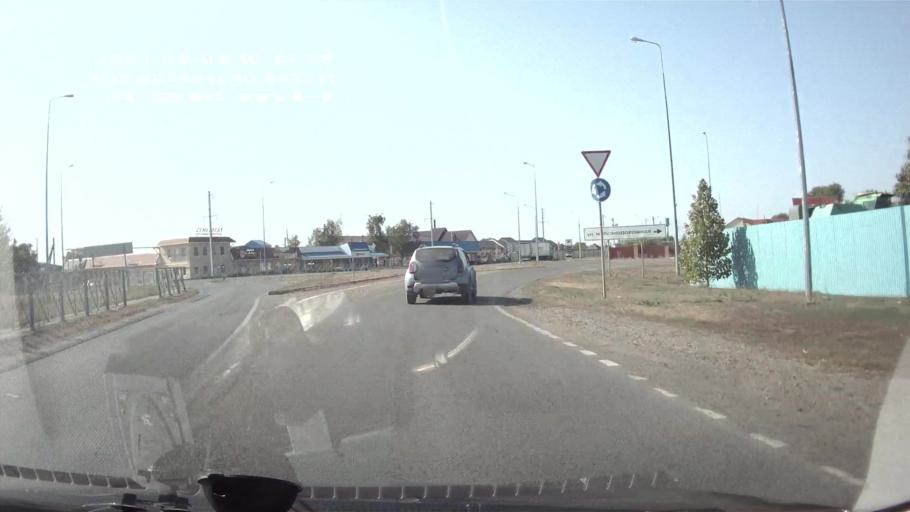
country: RU
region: Krasnodarskiy
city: Belaya Glina
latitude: 46.0944
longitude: 40.8431
